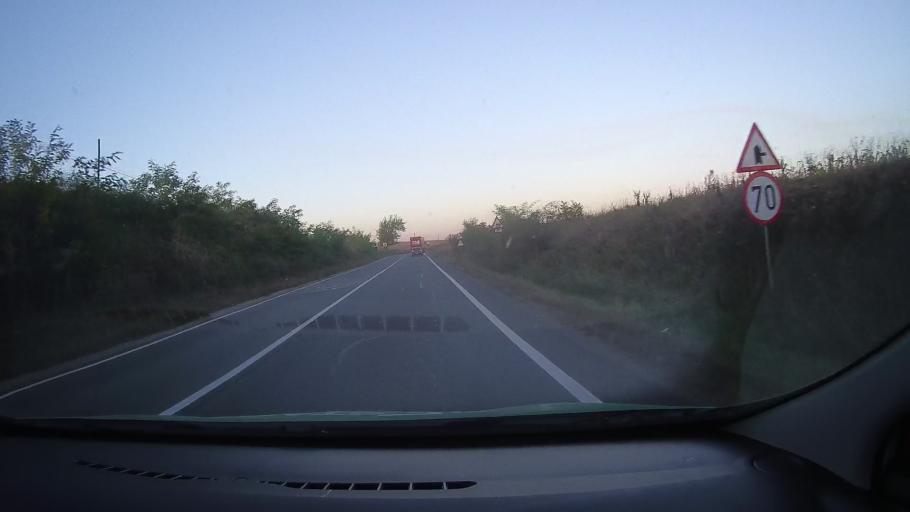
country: RO
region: Bihor
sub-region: Comuna Cherechiu
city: Cherechiu
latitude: 47.3652
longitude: 22.1198
